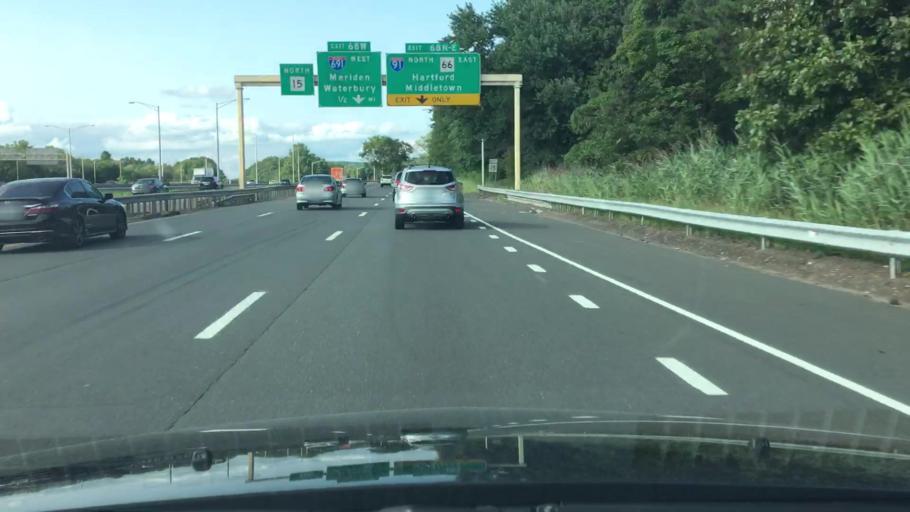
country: US
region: Connecticut
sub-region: New Haven County
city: Meriden
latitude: 41.5289
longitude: -72.7686
